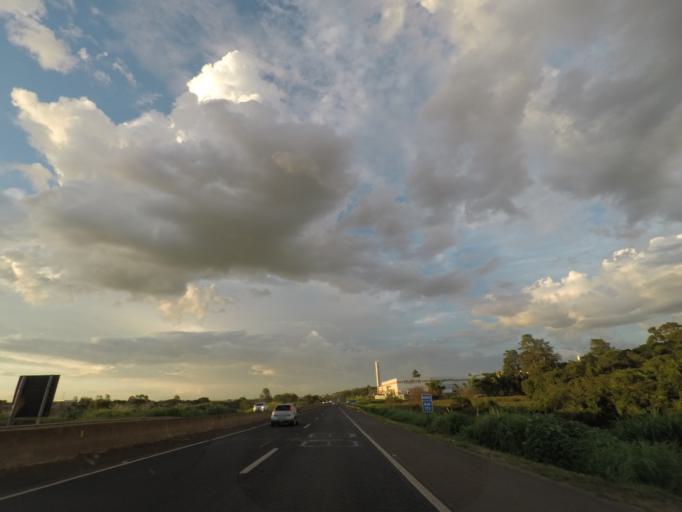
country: BR
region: Minas Gerais
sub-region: Uberaba
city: Uberaba
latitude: -19.7605
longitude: -47.9779
